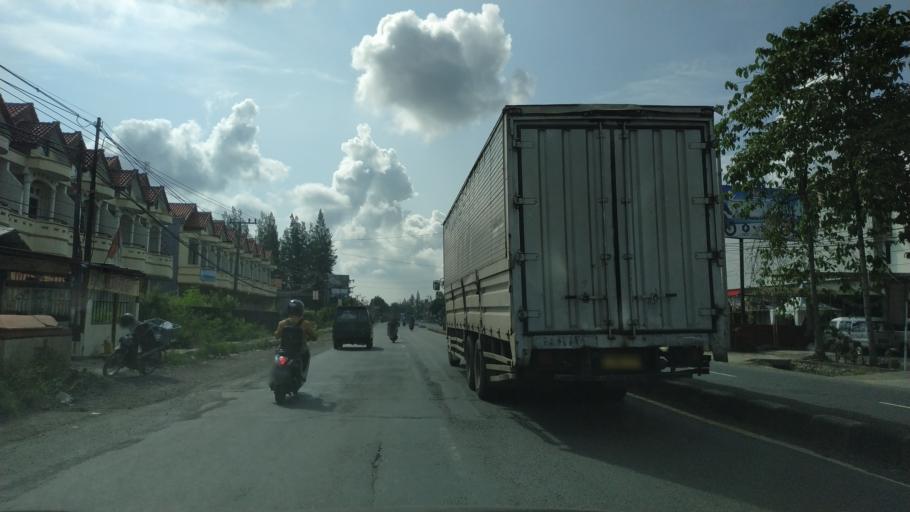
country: ID
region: Central Java
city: Comal
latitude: -6.8982
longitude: 109.5348
